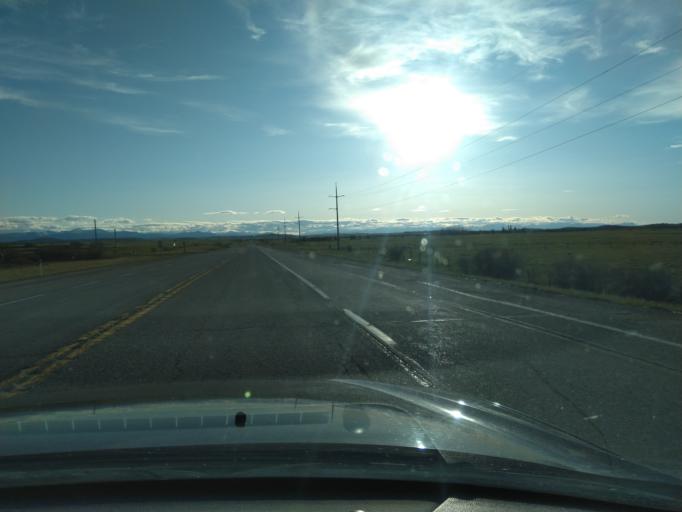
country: CA
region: Alberta
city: Cochrane
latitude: 51.0234
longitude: -114.3947
